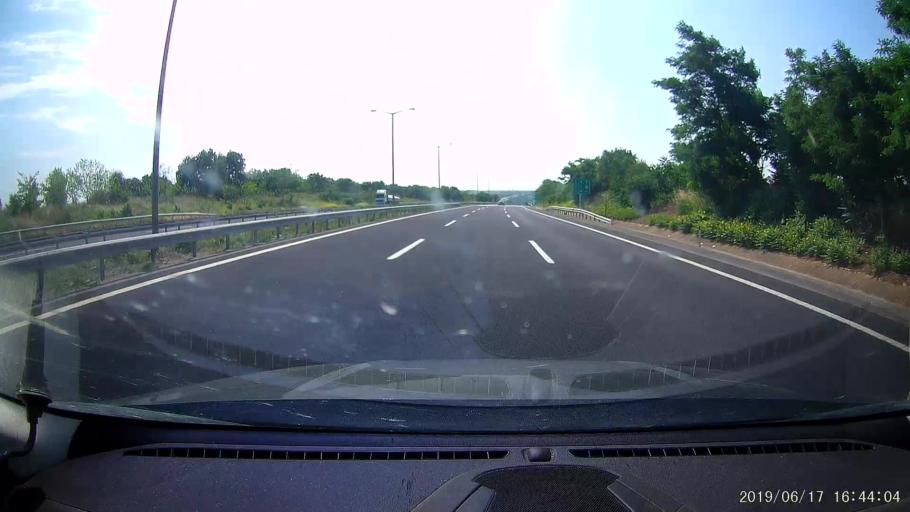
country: TR
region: Kirklareli
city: Luleburgaz
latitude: 41.4794
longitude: 27.2724
